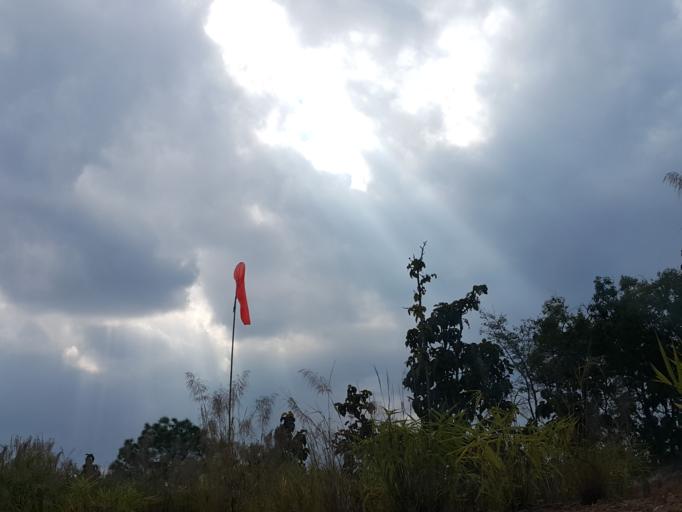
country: TH
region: Chiang Mai
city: Om Koi
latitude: 17.8047
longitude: 98.3612
